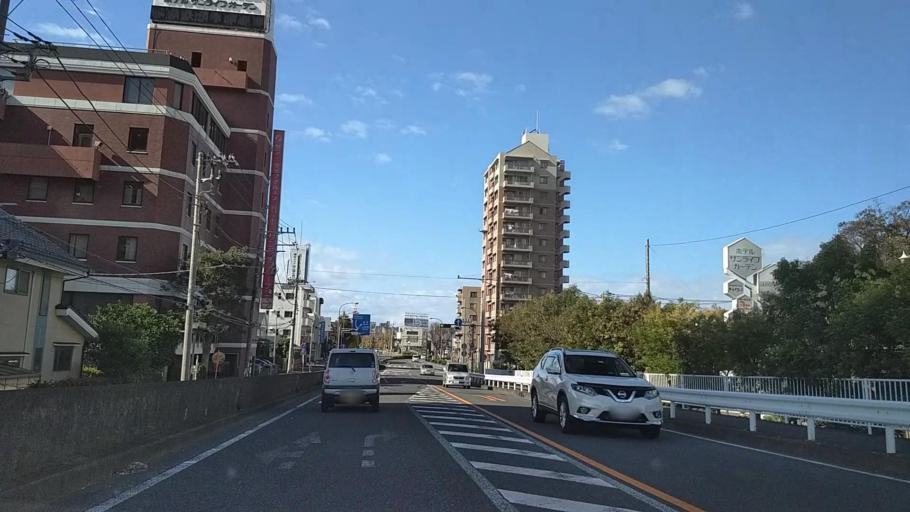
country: JP
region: Kanagawa
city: Hiratsuka
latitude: 35.3316
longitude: 139.3638
